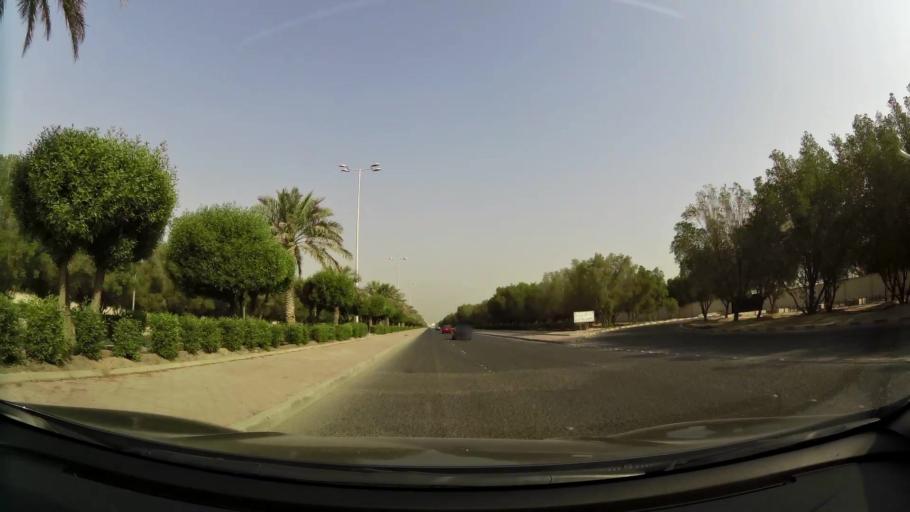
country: KW
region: Al Asimah
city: Ar Rabiyah
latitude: 29.3004
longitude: 47.8322
